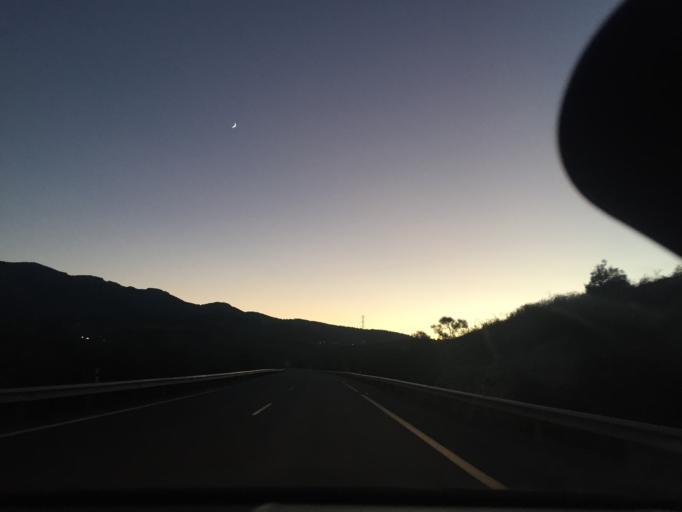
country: ES
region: Andalusia
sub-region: Provincia de Jaen
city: Jaen
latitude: 37.8017
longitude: -3.8200
